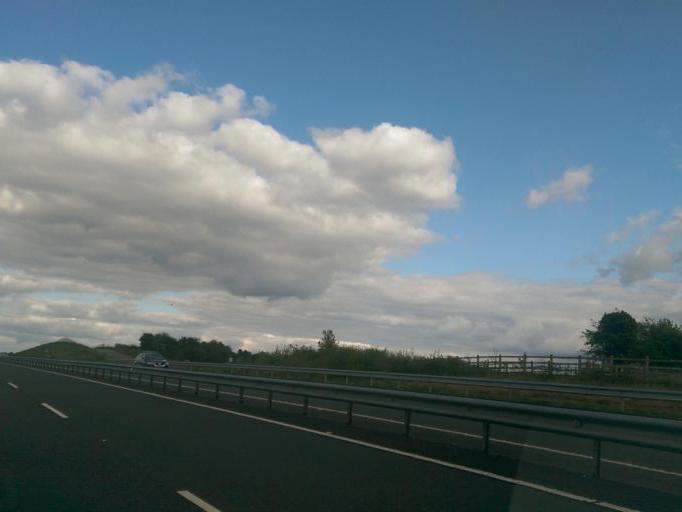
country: IE
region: Connaught
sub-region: County Galway
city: Ballinasloe
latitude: 53.3457
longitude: -8.0824
